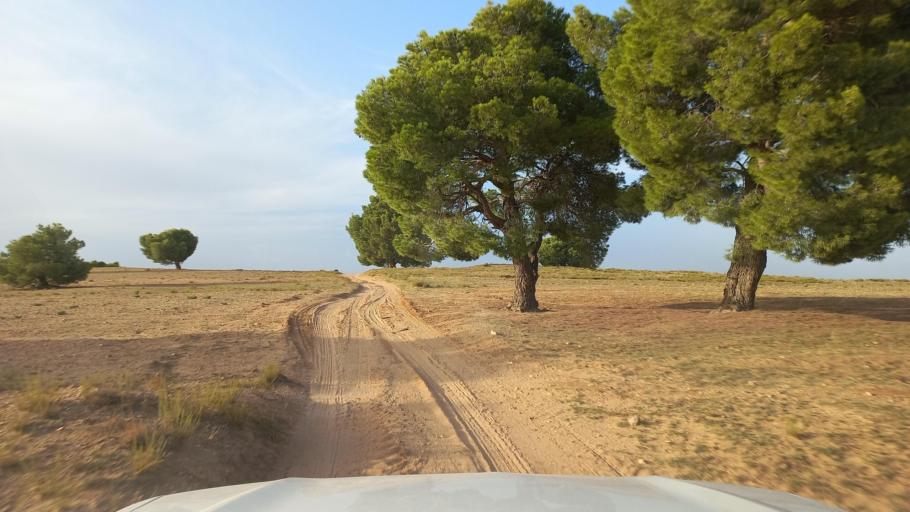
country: TN
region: Al Qasrayn
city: Sbiba
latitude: 35.4132
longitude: 8.8959
